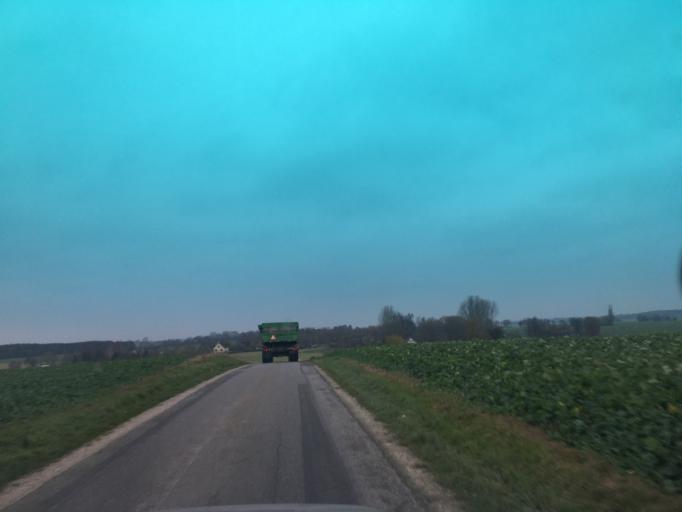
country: DK
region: Zealand
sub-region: Slagelse Kommune
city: Skaelskor
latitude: 55.2660
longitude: 11.4194
